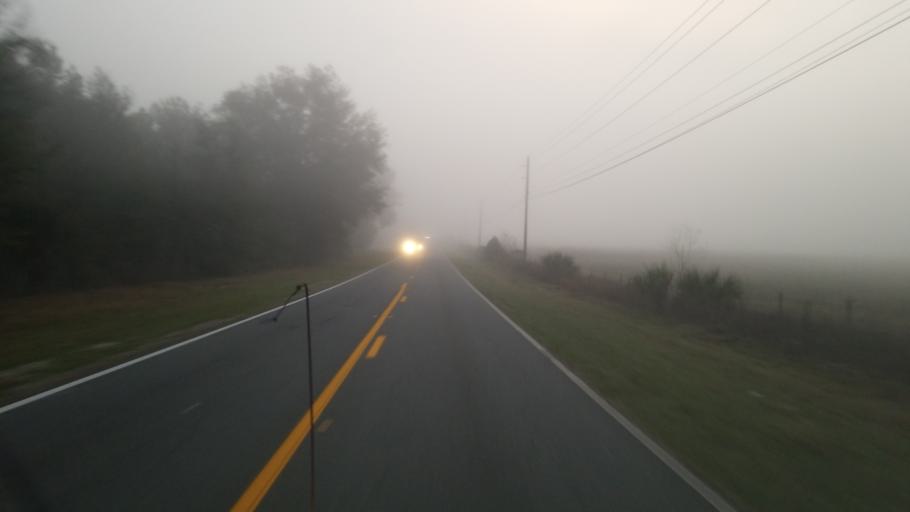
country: US
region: Florida
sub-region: Marion County
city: Ocala
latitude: 29.1502
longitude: -82.2446
